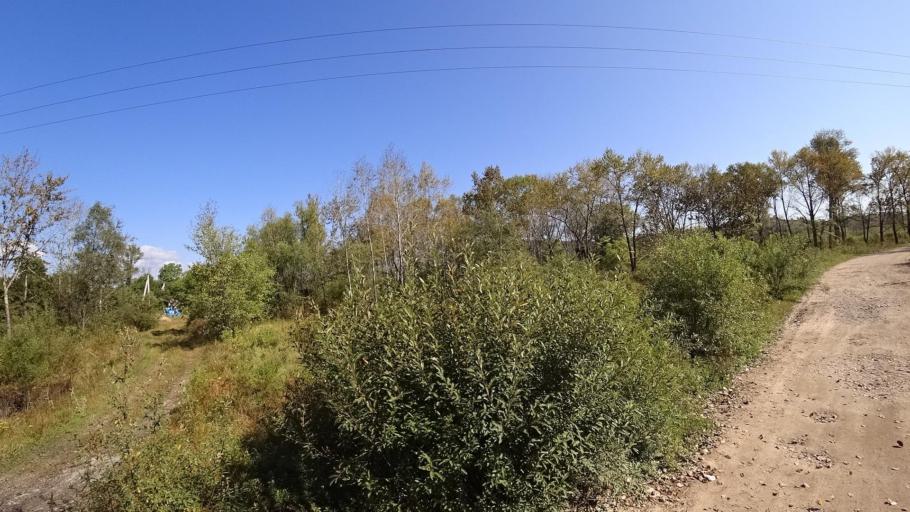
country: RU
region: Jewish Autonomous Oblast
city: Bira
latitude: 49.0021
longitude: 132.4496
